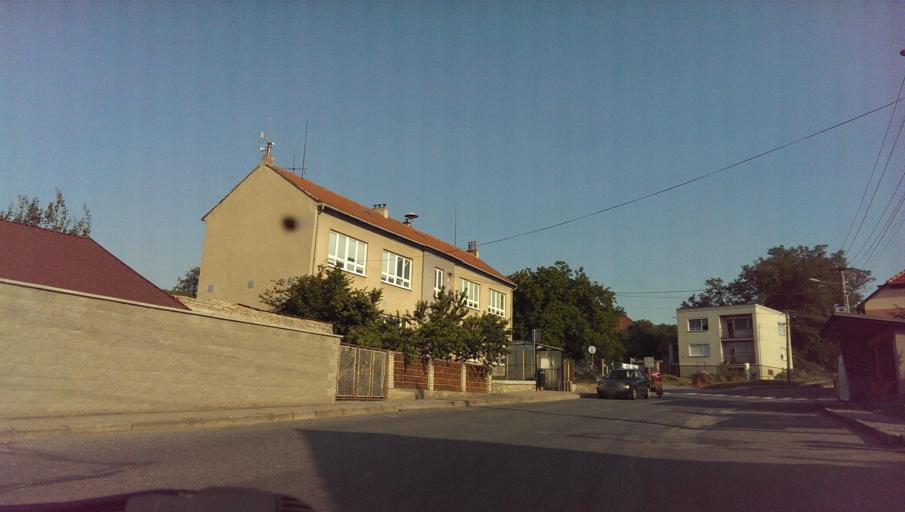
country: CZ
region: South Moravian
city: Nesovice
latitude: 49.1328
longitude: 17.1063
